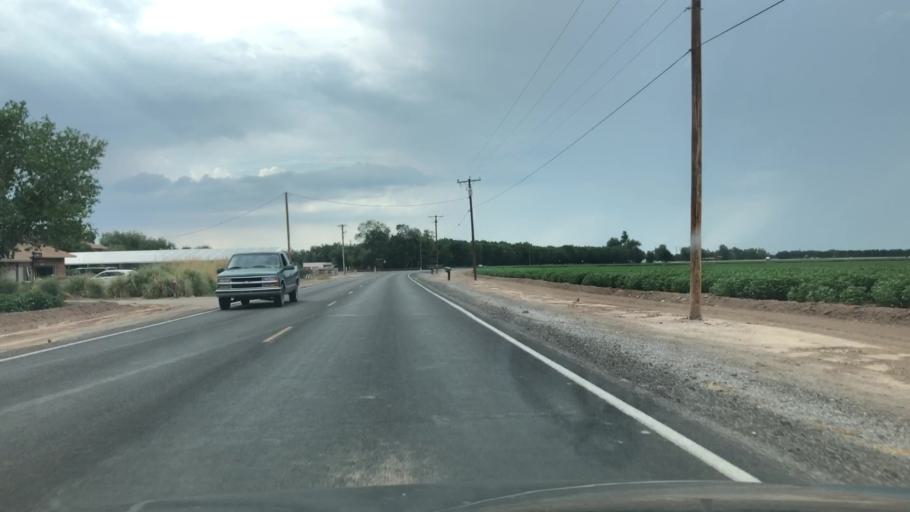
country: US
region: New Mexico
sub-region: Dona Ana County
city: La Union
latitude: 31.9685
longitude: -106.6507
